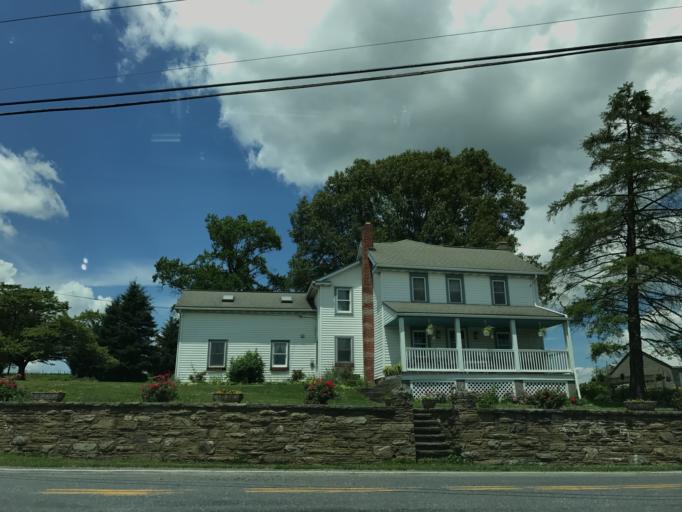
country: US
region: Pennsylvania
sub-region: Lancaster County
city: Mountville
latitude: 39.9612
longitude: -76.4374
